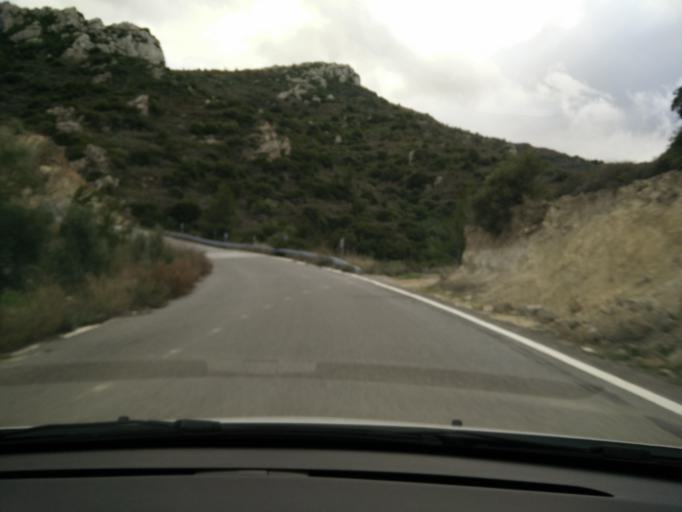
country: GR
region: Crete
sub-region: Nomos Lasithiou
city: Gra Liyia
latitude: 35.0917
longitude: 25.6915
